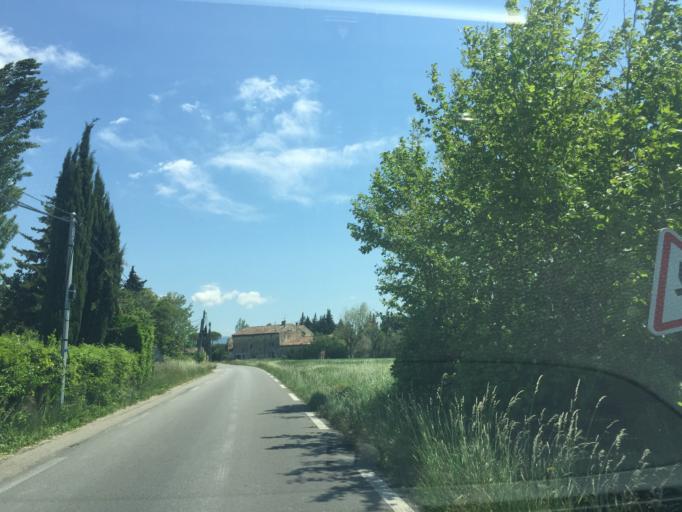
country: FR
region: Provence-Alpes-Cote d'Azur
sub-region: Departement du Vaucluse
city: Althen-des-Paluds
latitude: 43.9989
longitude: 4.9606
